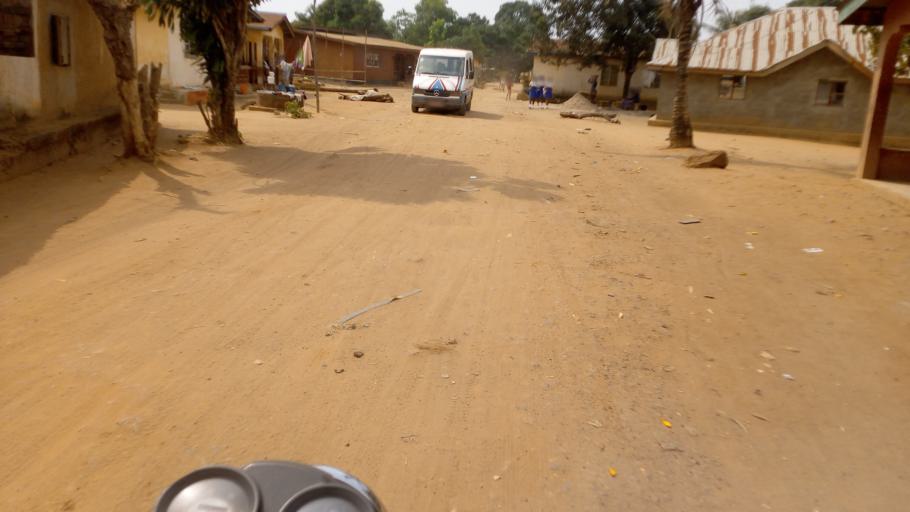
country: SL
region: Western Area
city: Waterloo
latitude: 8.3225
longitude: -13.0558
